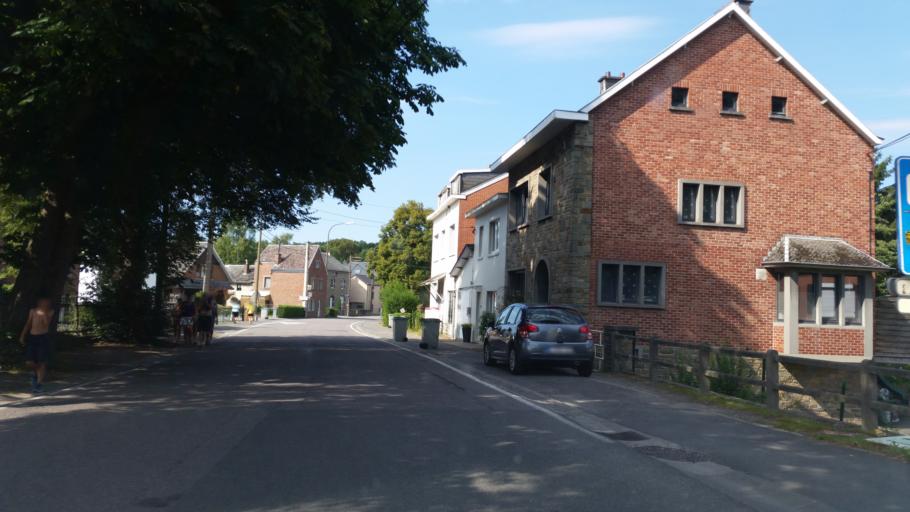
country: BE
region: Wallonia
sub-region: Province du Luxembourg
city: Durbuy
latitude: 50.3527
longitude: 5.4938
